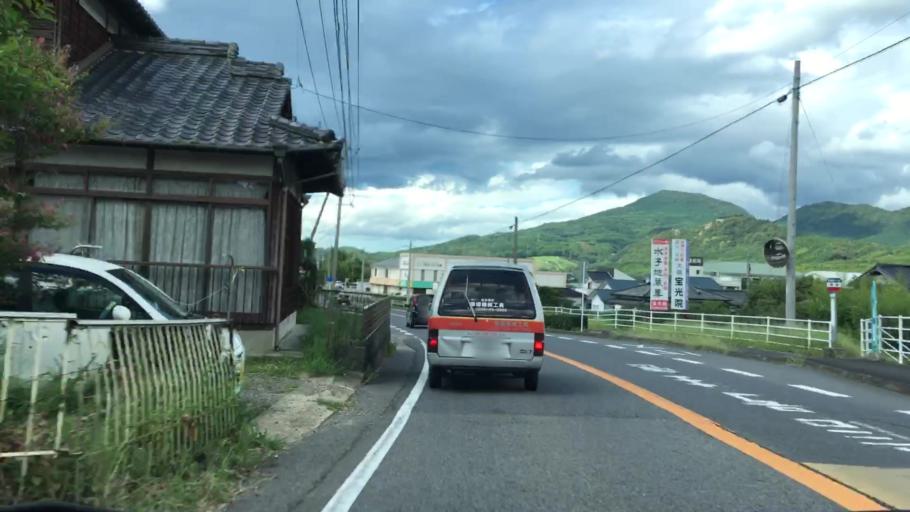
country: JP
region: Saga Prefecture
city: Imaricho-ko
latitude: 33.2057
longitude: 129.8504
